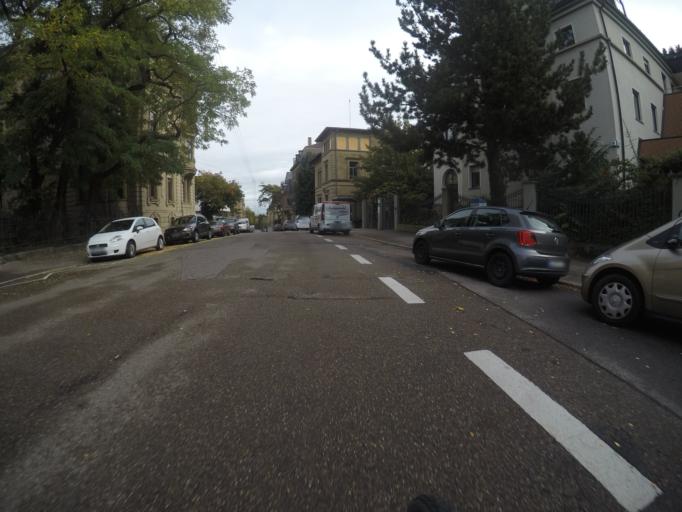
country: DE
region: Baden-Wuerttemberg
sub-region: Regierungsbezirk Stuttgart
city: Stuttgart
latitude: 48.7664
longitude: 9.1672
